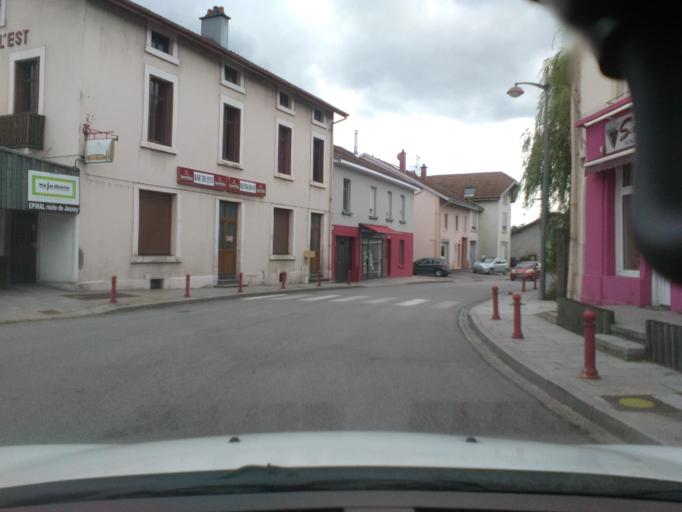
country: FR
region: Lorraine
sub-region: Departement des Vosges
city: Bruyeres
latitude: 48.1725
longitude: 6.6716
